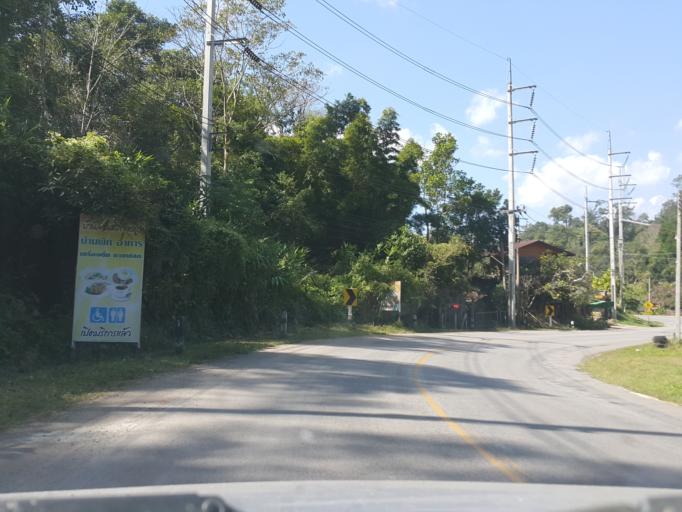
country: TH
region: Chiang Mai
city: Mae Taeng
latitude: 19.1167
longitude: 98.7291
